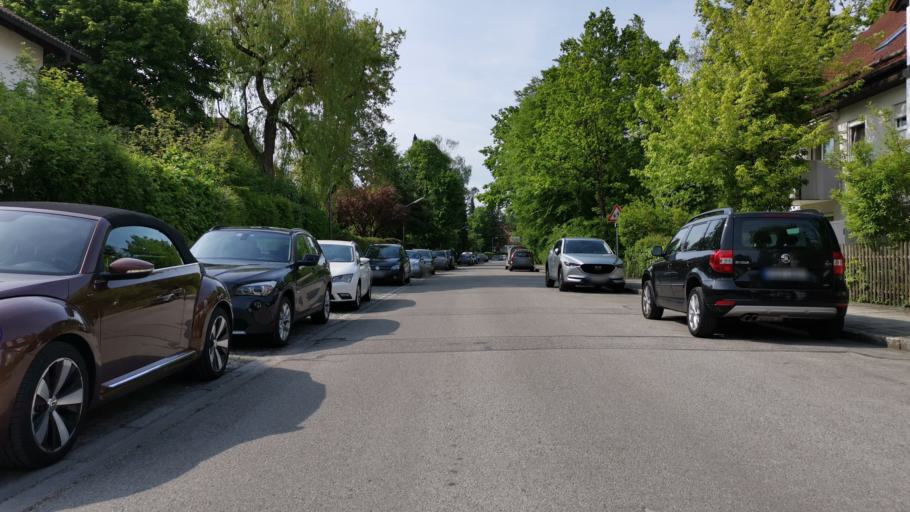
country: DE
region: Bavaria
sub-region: Upper Bavaria
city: Pullach im Isartal
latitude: 48.0854
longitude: 11.5215
